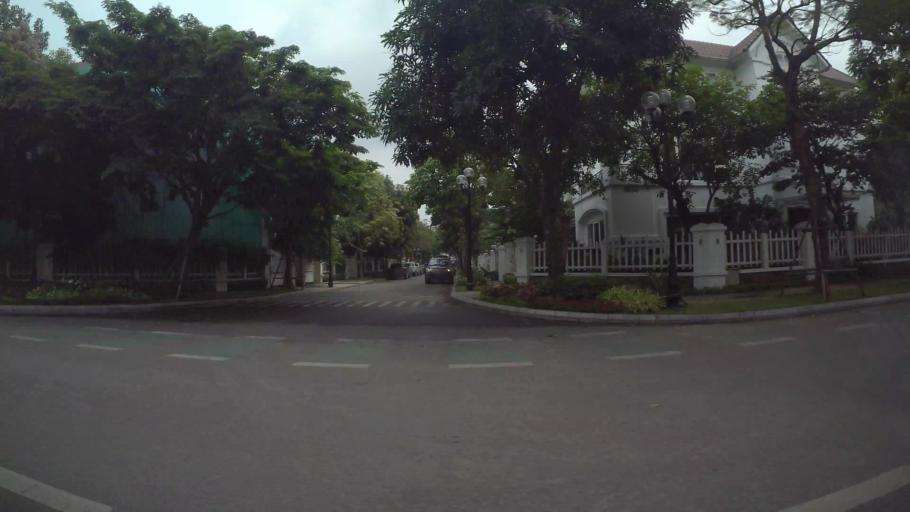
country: VN
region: Ha Noi
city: Trau Quy
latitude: 21.0539
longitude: 105.9136
